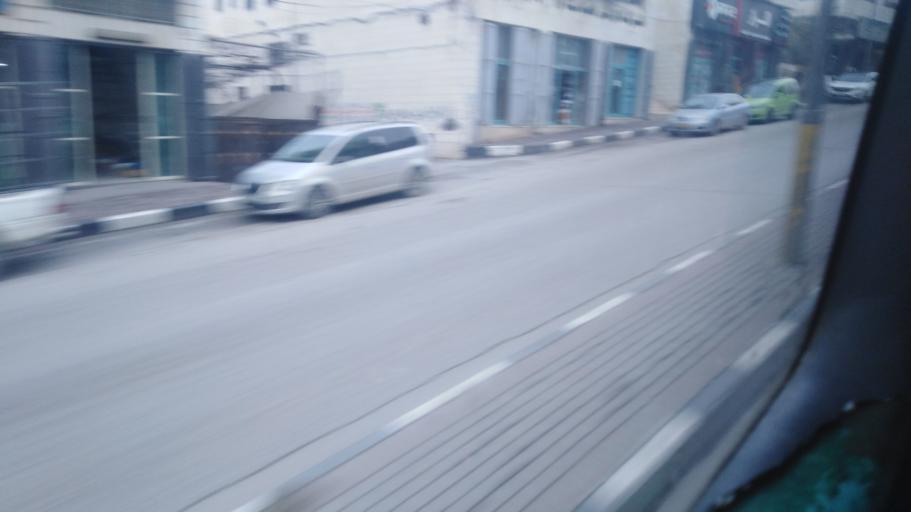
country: PS
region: West Bank
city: Hebron
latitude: 31.5280
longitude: 35.0886
